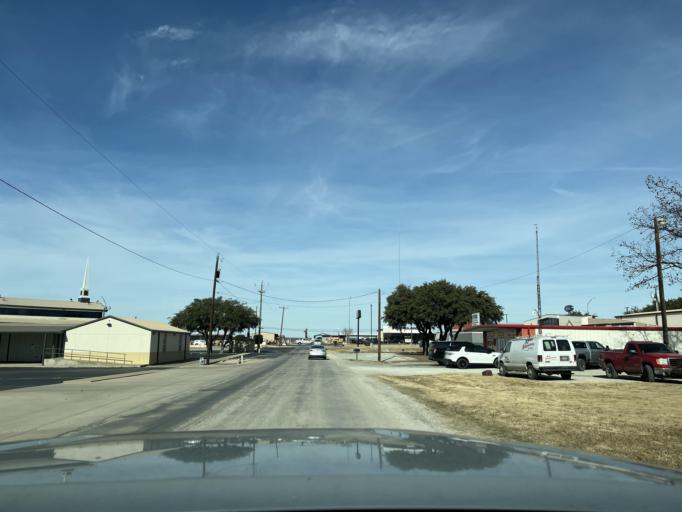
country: US
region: Texas
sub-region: Eastland County
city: Eastland
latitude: 32.4003
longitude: -98.7978
